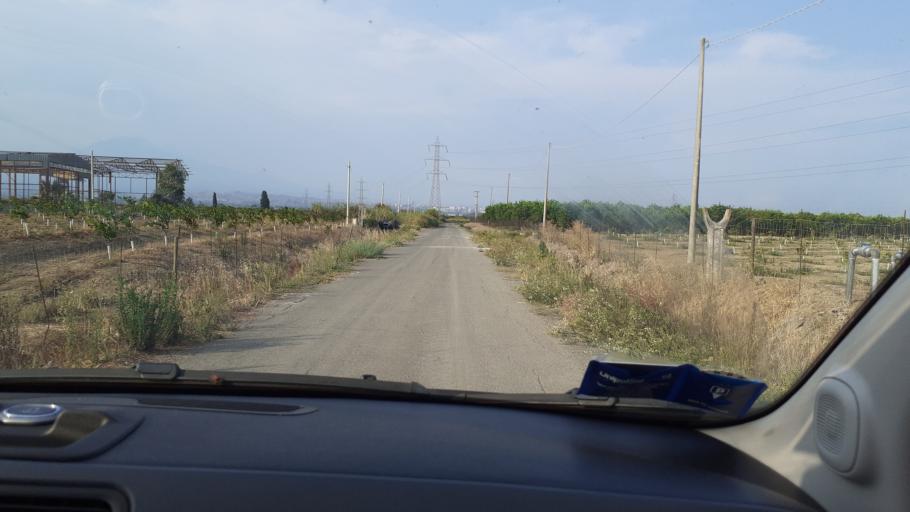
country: IT
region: Sicily
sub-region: Catania
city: Catania
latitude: 37.4228
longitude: 15.0087
